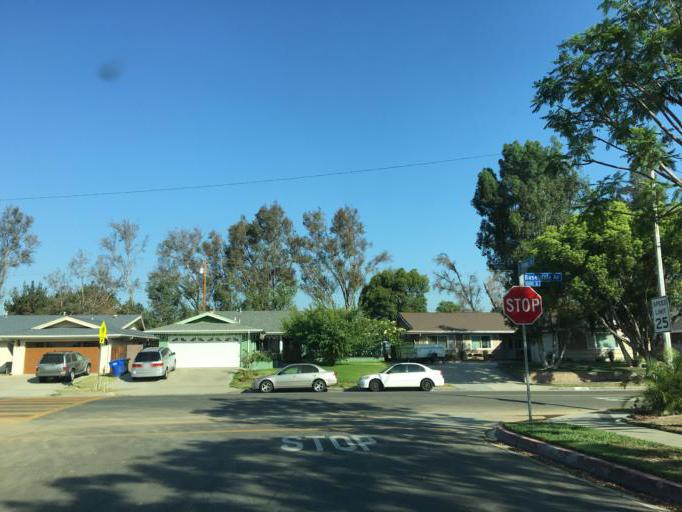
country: US
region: California
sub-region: Los Angeles County
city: Avocado Heights
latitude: 34.0391
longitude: -118.0099
